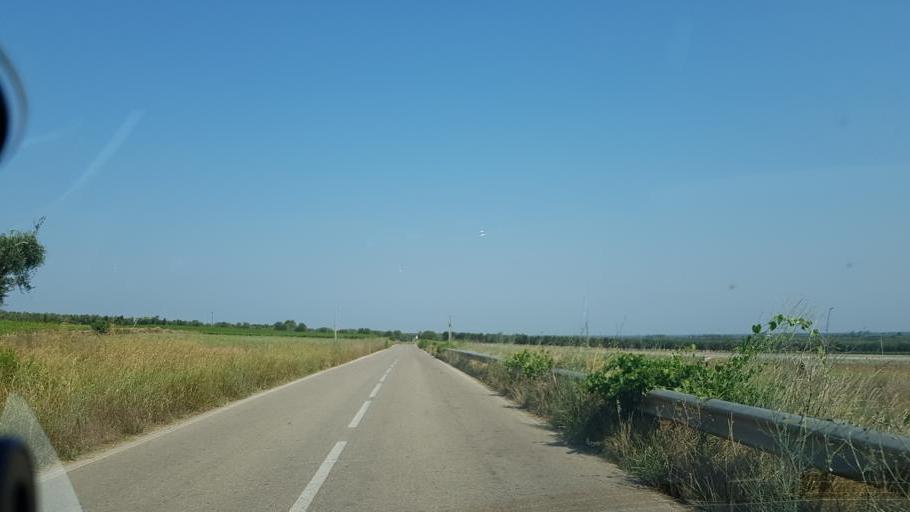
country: IT
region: Apulia
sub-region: Provincia di Brindisi
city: Torre Santa Susanna
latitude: 40.4986
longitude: 17.7256
